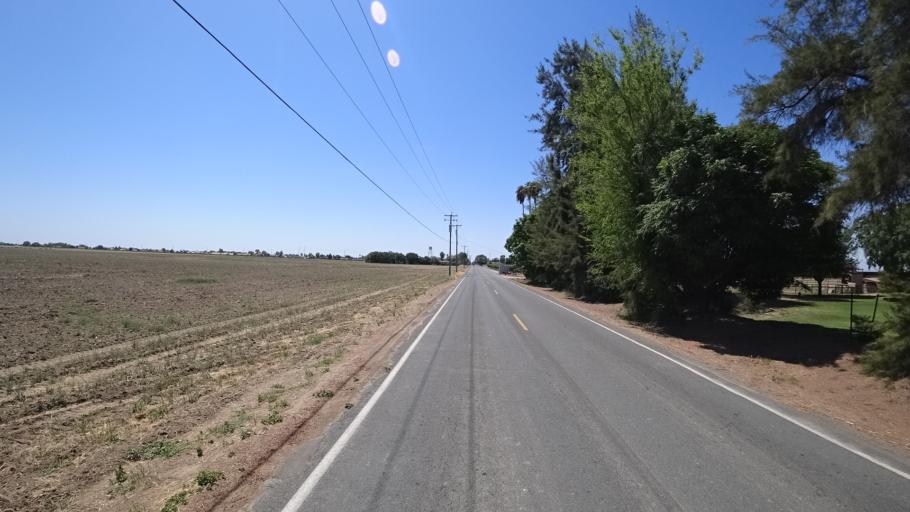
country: US
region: California
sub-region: Kings County
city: Lemoore
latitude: 36.2462
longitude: -119.7629
